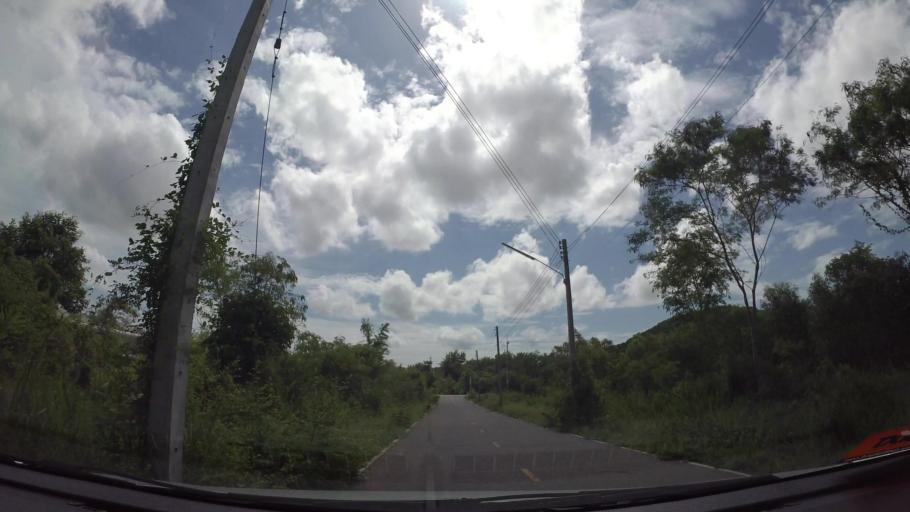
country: TH
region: Chon Buri
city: Sattahip
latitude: 12.6967
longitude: 100.9029
